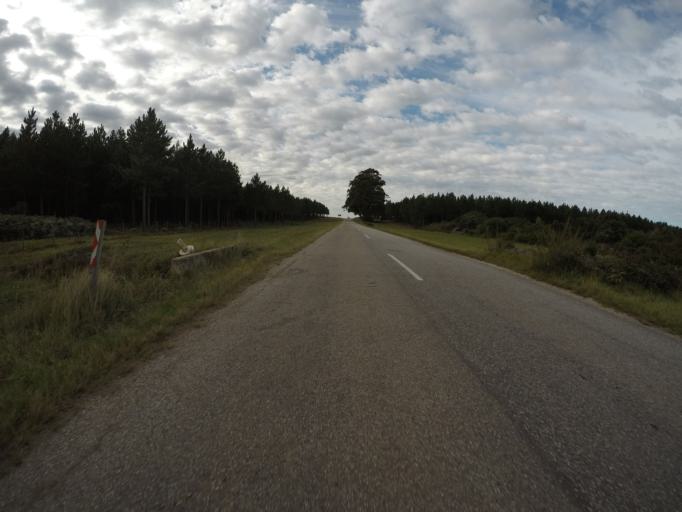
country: ZA
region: Eastern Cape
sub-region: Cacadu District Municipality
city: Kareedouw
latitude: -34.0284
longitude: 24.3752
